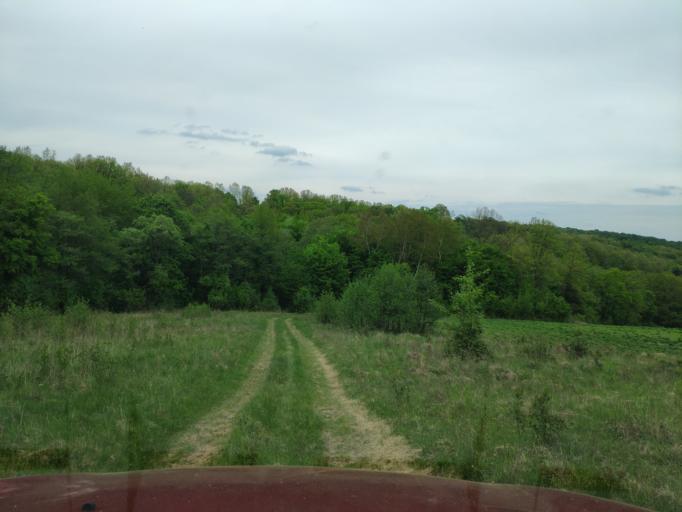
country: SK
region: Banskobystricky
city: Revuca
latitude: 48.5174
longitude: 20.1439
